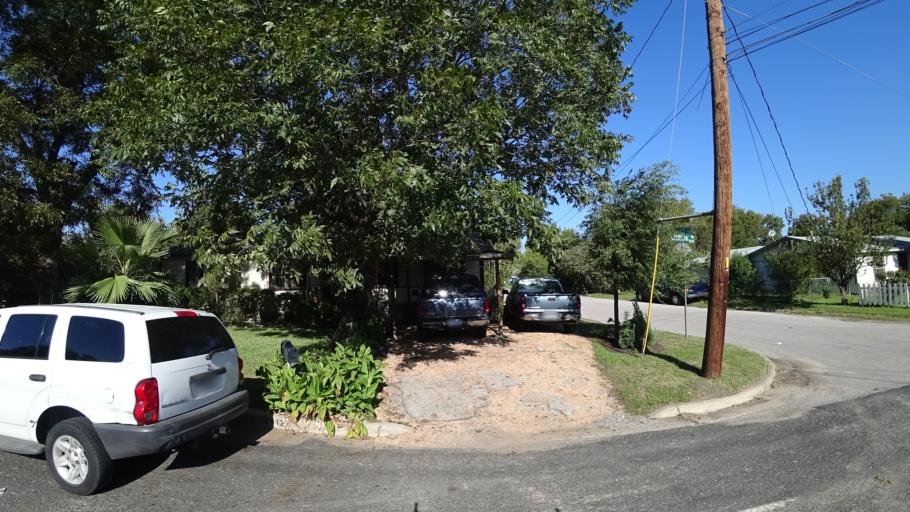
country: US
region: Texas
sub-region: Travis County
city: Austin
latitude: 30.3510
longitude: -97.7009
